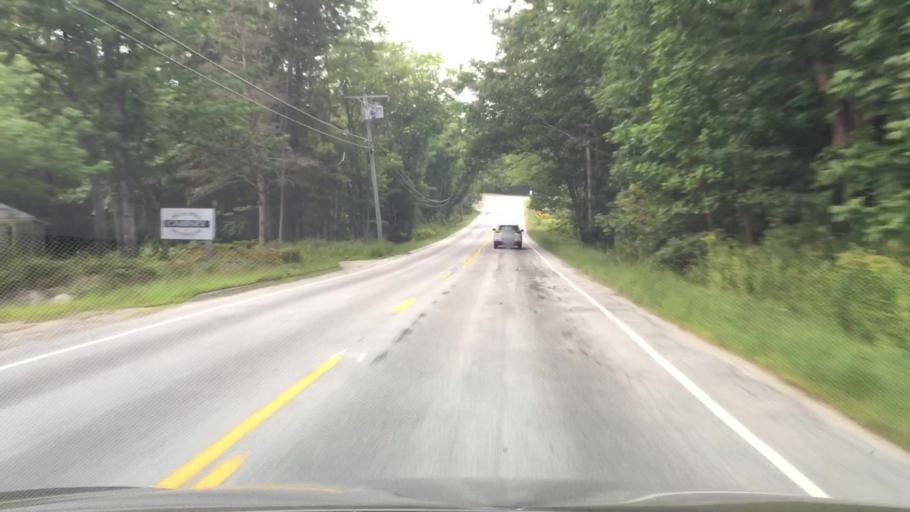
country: US
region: Maine
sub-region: Hancock County
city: Penobscot
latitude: 44.4340
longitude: -68.6059
